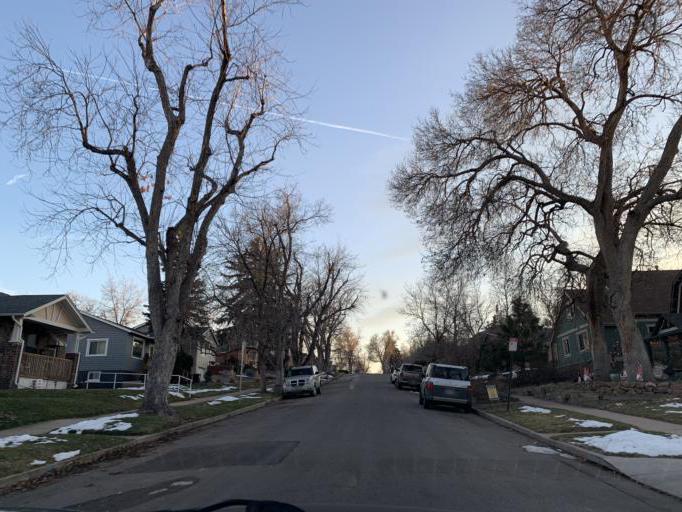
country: US
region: Colorado
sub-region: Adams County
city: Berkley
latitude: 39.7902
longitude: -105.0428
